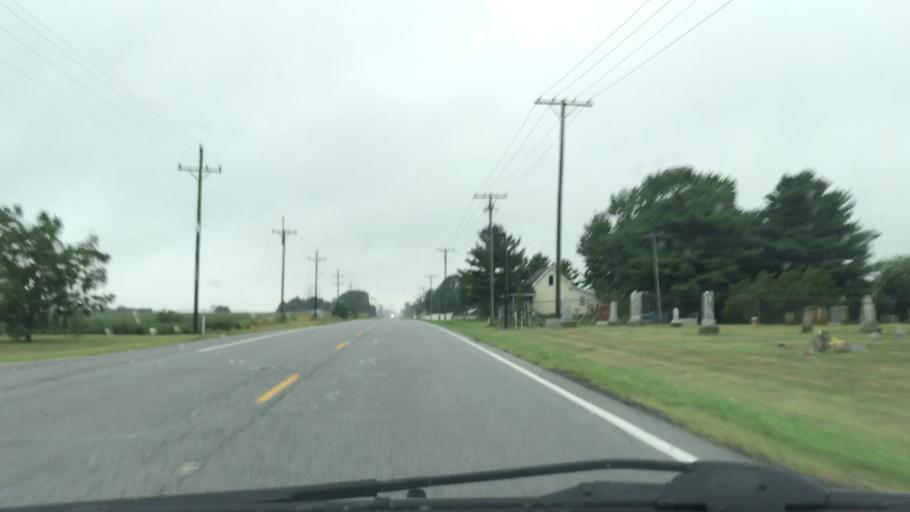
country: US
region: Indiana
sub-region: Hamilton County
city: Sheridan
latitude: 40.1286
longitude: -86.2991
